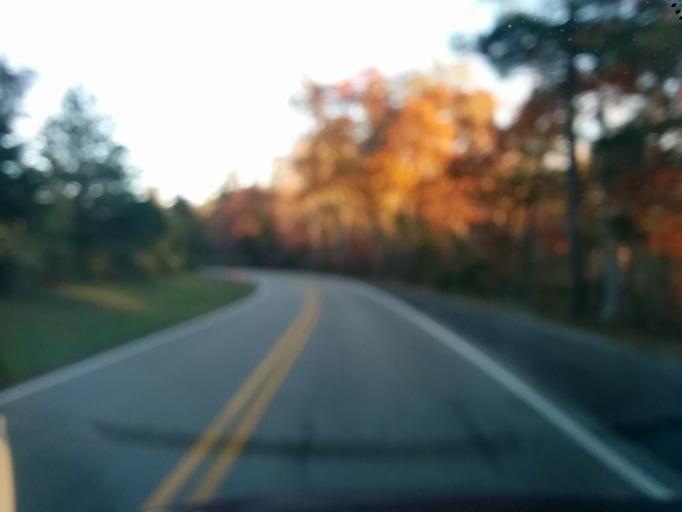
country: US
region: Virginia
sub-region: Rockbridge County
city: East Lexington
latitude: 37.9119
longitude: -79.4288
